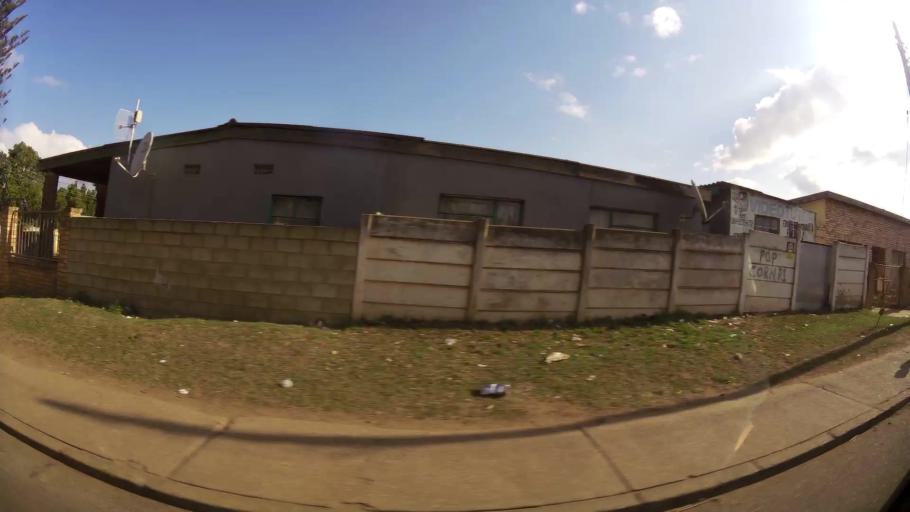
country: ZA
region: Eastern Cape
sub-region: Nelson Mandela Bay Metropolitan Municipality
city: Uitenhage
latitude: -33.7380
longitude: 25.3712
